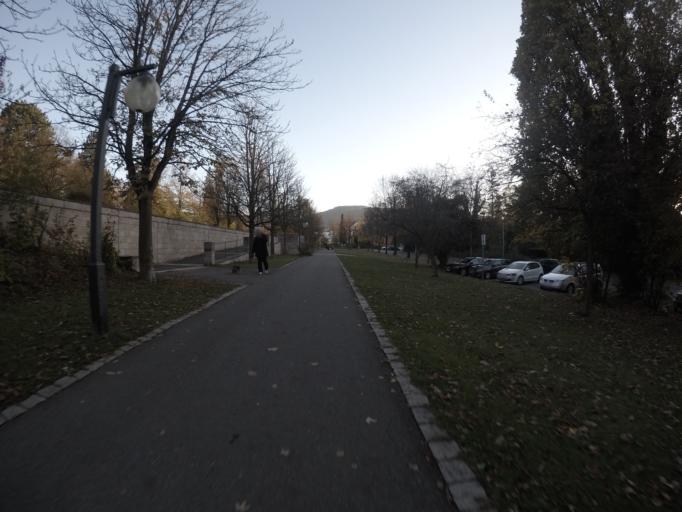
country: DE
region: Baden-Wuerttemberg
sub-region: Tuebingen Region
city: Pfullingen
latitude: 48.4671
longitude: 9.2288
